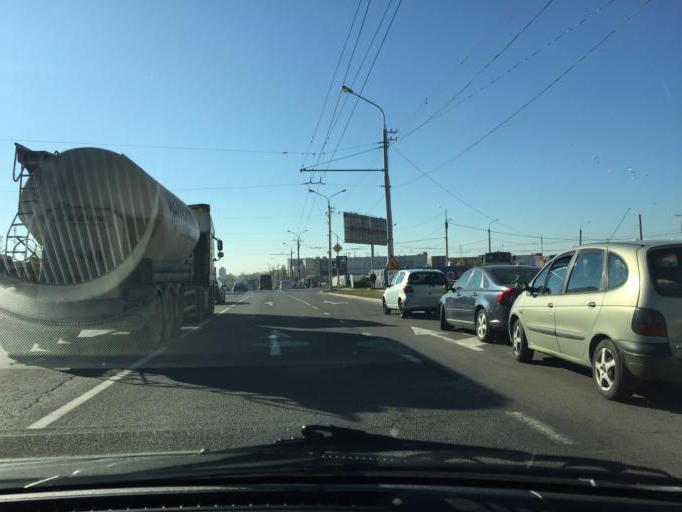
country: BY
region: Minsk
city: Syenitsa
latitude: 53.8444
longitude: 27.5343
